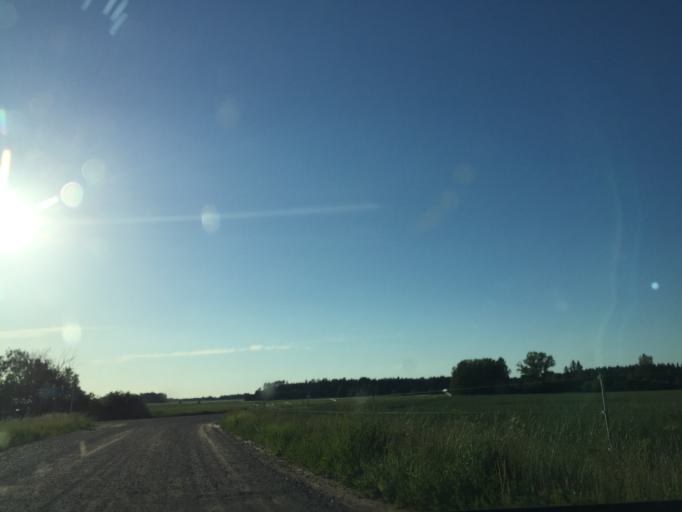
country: LV
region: Talsu Rajons
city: Sabile
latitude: 56.8773
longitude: 22.6118
